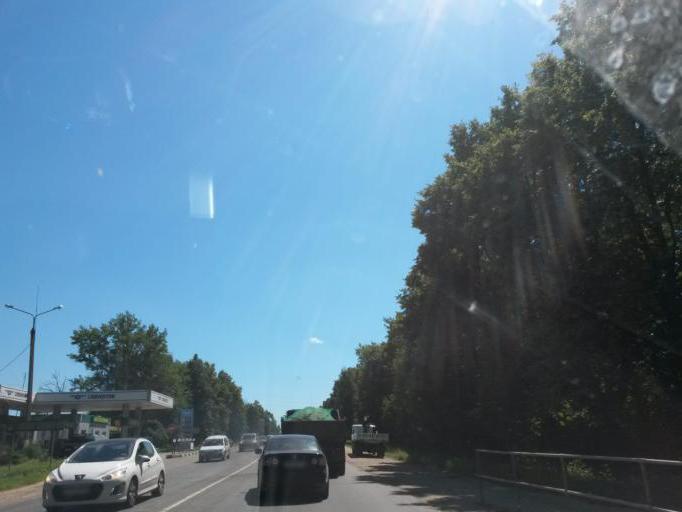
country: RU
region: Moskovskaya
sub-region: Chekhovskiy Rayon
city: Chekhov
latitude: 55.1280
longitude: 37.4510
